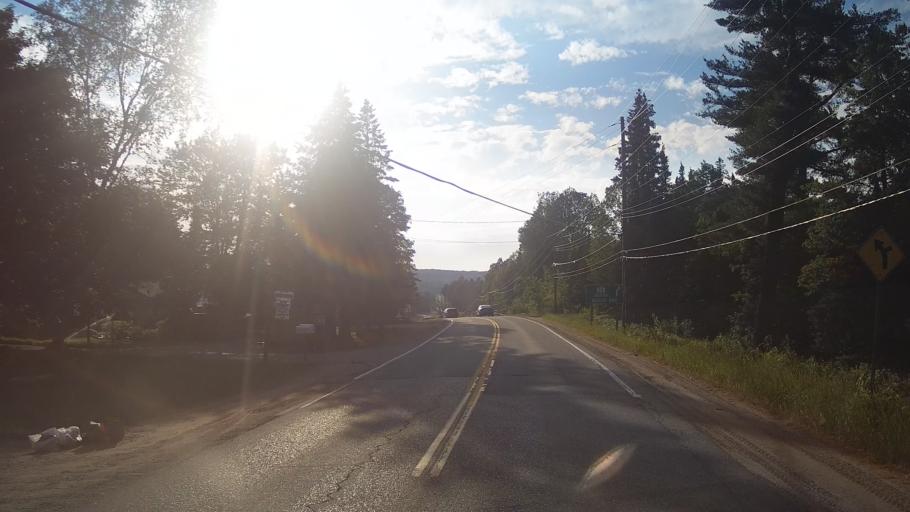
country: CA
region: Ontario
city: Huntsville
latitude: 45.3728
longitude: -79.2102
